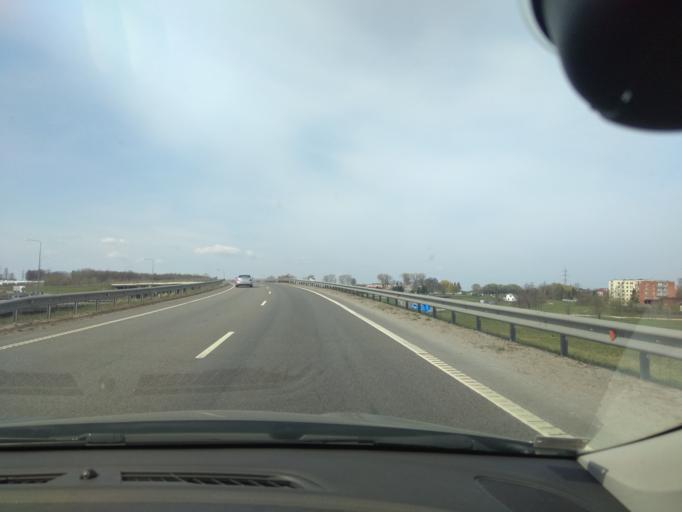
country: LT
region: Kauno apskritis
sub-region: Kaunas
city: Silainiai
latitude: 54.9396
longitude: 23.8852
